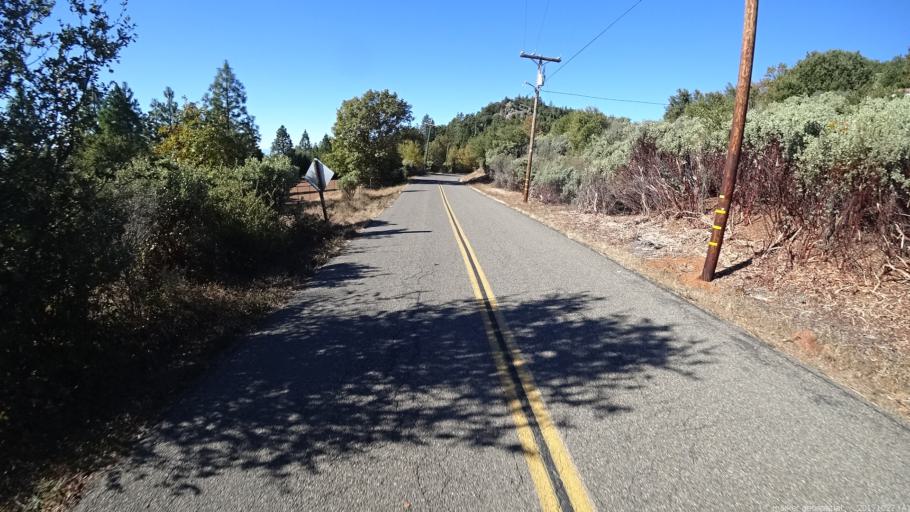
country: US
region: California
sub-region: Shasta County
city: Shingletown
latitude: 40.6549
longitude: -121.8801
